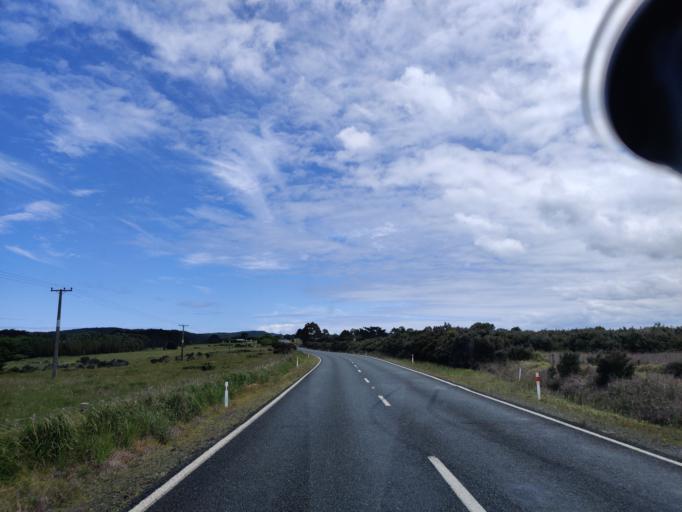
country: NZ
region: Northland
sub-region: Far North District
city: Kaitaia
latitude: -34.6727
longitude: 172.9951
